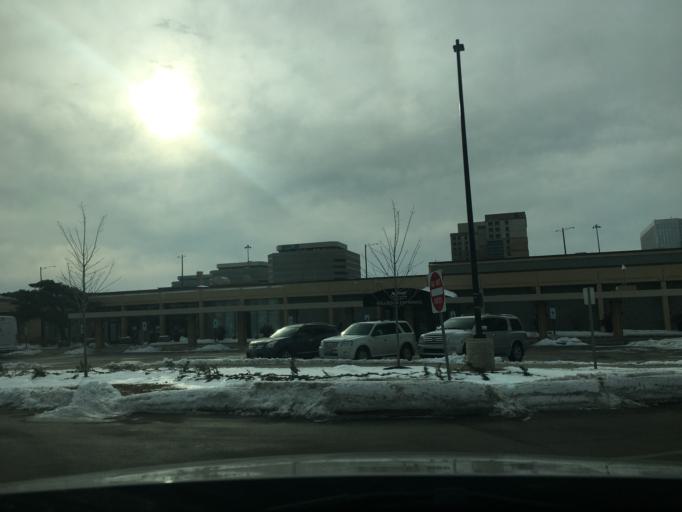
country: US
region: Illinois
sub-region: Cook County
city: Park Ridge
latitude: 41.9861
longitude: -87.8413
